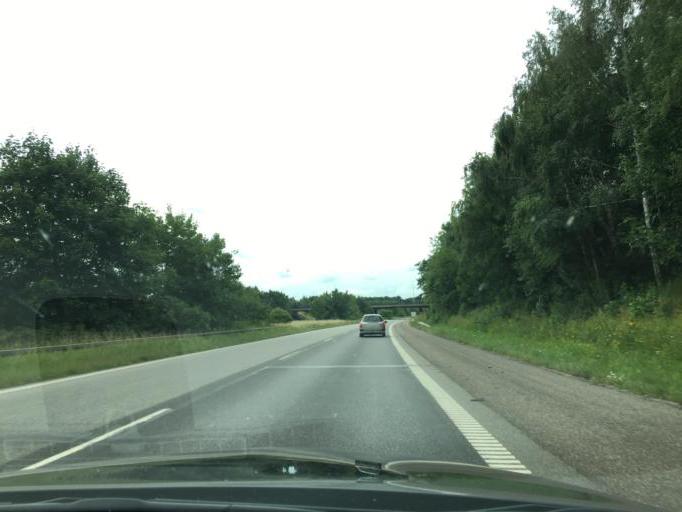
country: DK
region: Capital Region
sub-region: Fureso Kommune
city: Stavnsholt
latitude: 55.8180
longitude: 12.3831
